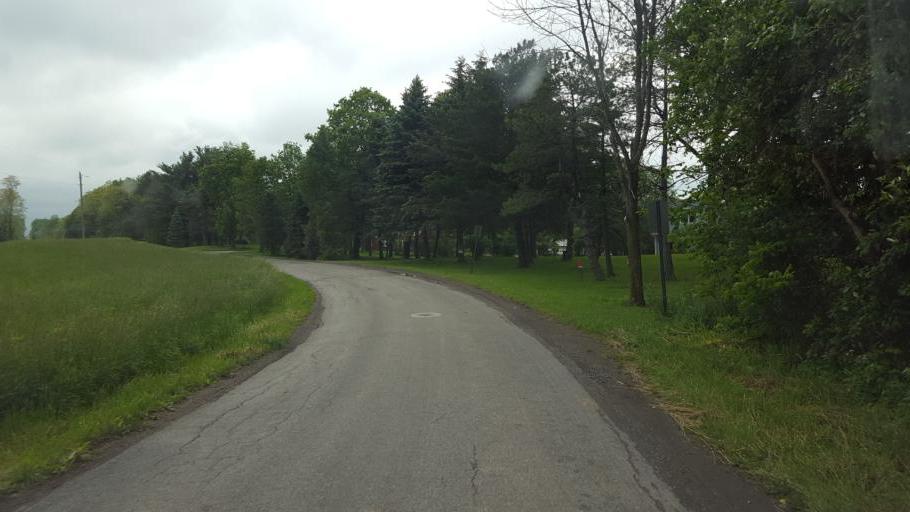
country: US
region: Ohio
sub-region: Wayne County
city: West Salem
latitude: 40.9354
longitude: -82.1808
